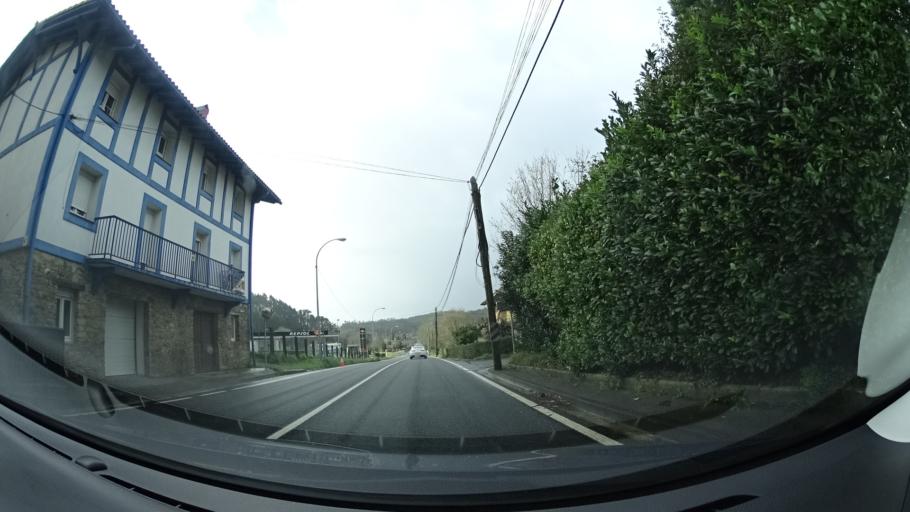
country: ES
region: Basque Country
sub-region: Bizkaia
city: Mungia
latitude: 43.3718
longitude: -2.8048
